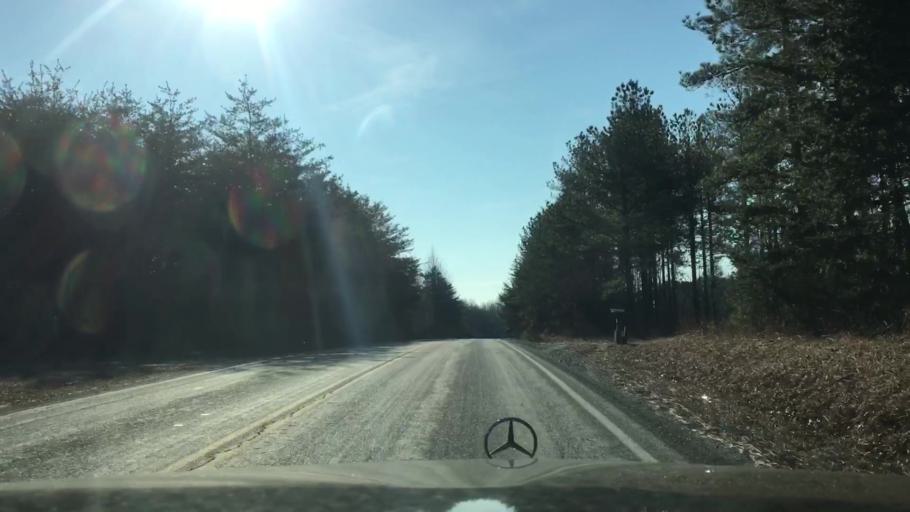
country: US
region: Virginia
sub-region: Pittsylvania County
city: Motley
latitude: 37.1803
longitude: -79.4103
